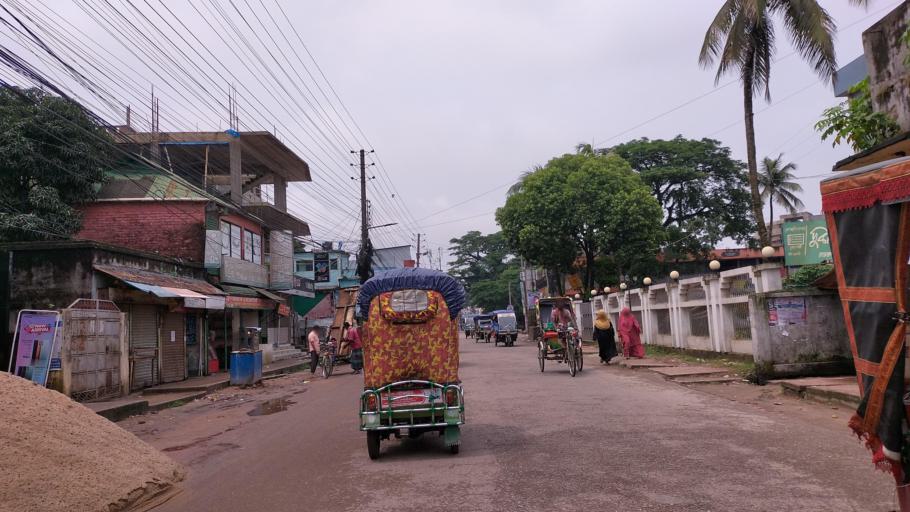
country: BD
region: Dhaka
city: Netrakona
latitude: 24.8776
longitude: 90.7306
